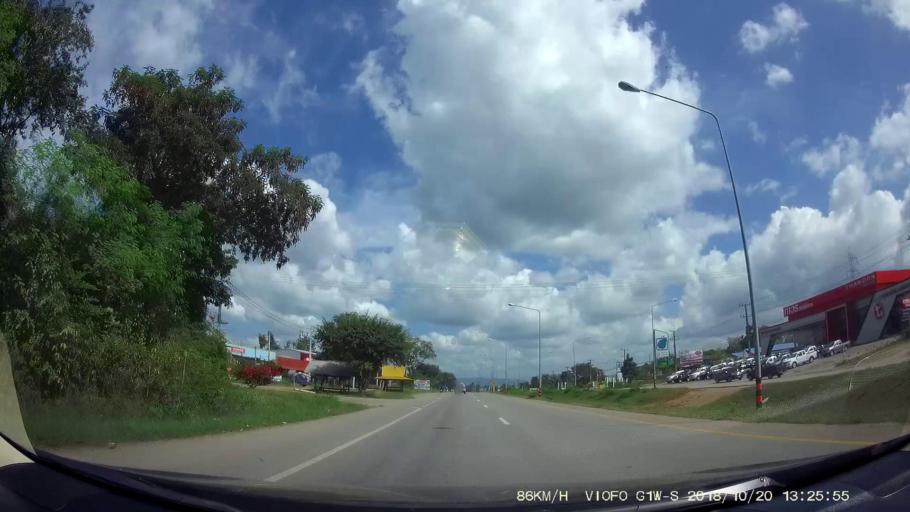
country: TH
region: Chaiyaphum
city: Khon San
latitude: 16.5944
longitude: 101.9388
